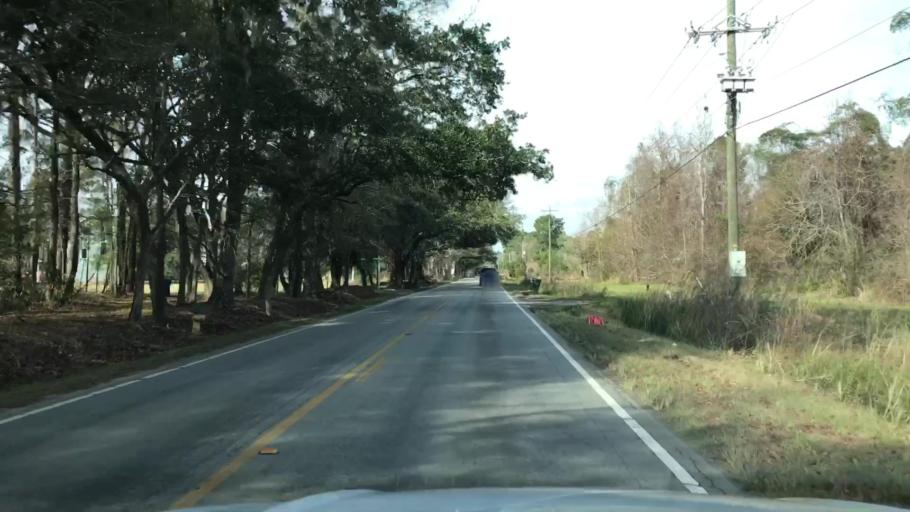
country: US
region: South Carolina
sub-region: Charleston County
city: Shell Point
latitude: 32.7581
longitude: -80.0539
